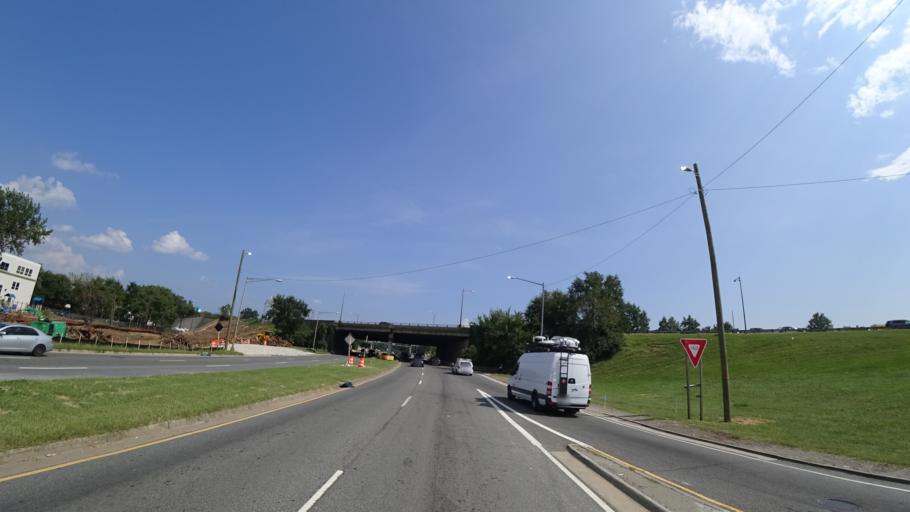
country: US
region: Maryland
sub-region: Prince George's County
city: Glassmanor
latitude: 38.8635
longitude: -77.0006
